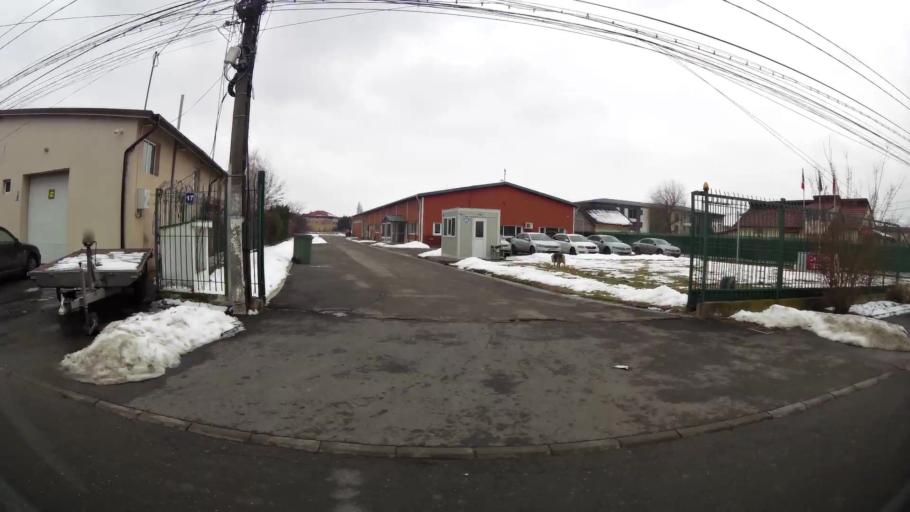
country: RO
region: Ilfov
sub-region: Comuna Otopeni
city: Otopeni
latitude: 44.5539
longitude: 26.0801
